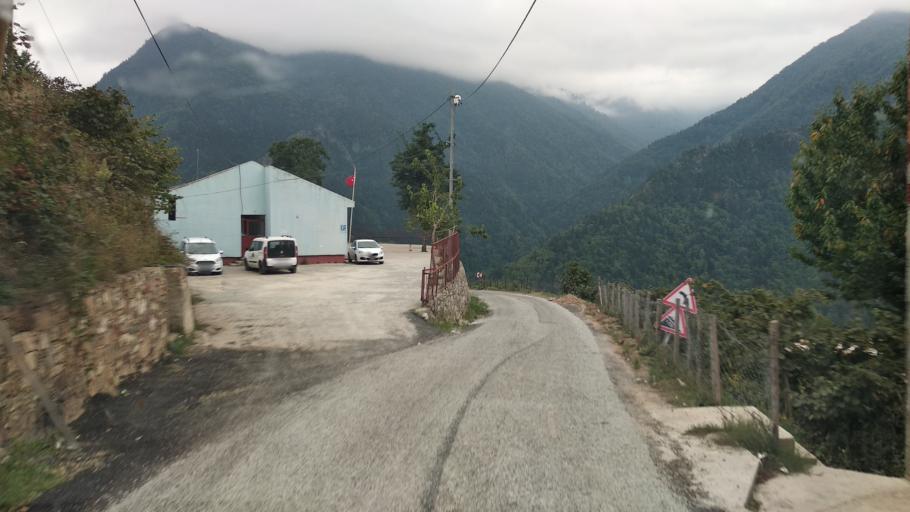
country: TR
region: Giresun
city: Dogankent
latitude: 40.7438
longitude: 38.9914
